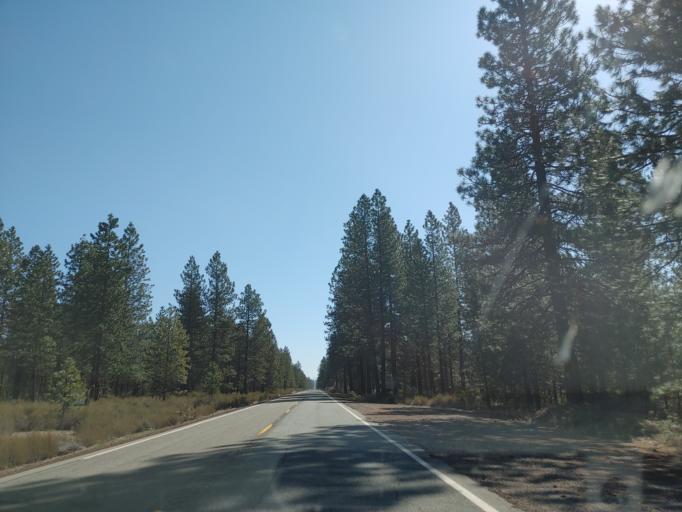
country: US
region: California
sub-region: Siskiyou County
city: McCloud
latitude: 41.2523
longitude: -122.1063
